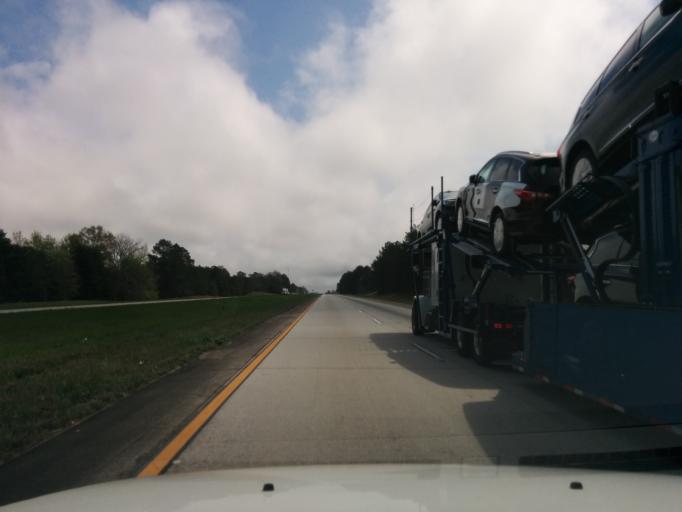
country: US
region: Georgia
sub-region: Candler County
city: Metter
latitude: 32.3672
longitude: -82.0134
